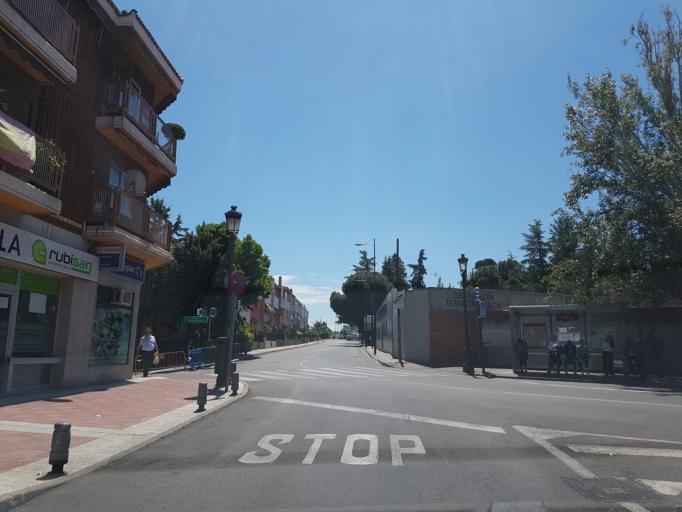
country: ES
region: Madrid
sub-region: Provincia de Madrid
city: Pozuelo de Alarcon
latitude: 40.4341
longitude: -3.8132
